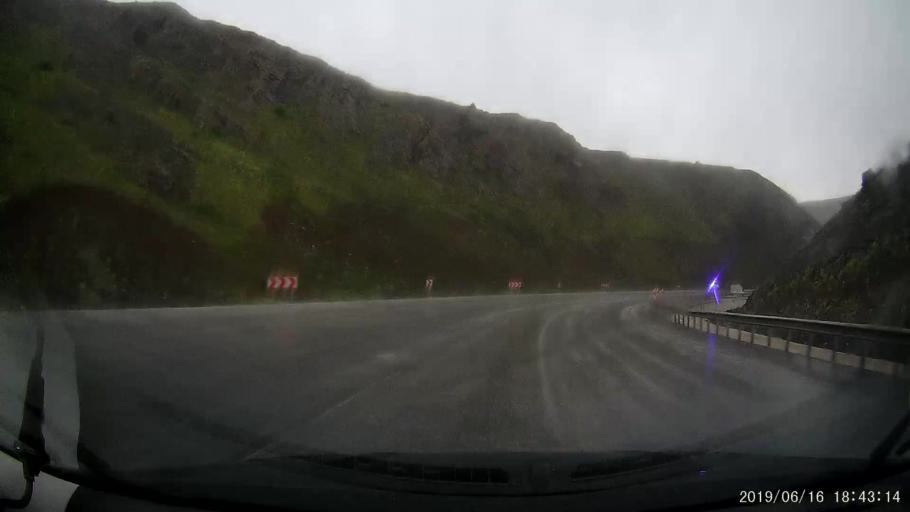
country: TR
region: Erzincan
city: Doganbeyli
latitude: 39.8677
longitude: 39.0933
